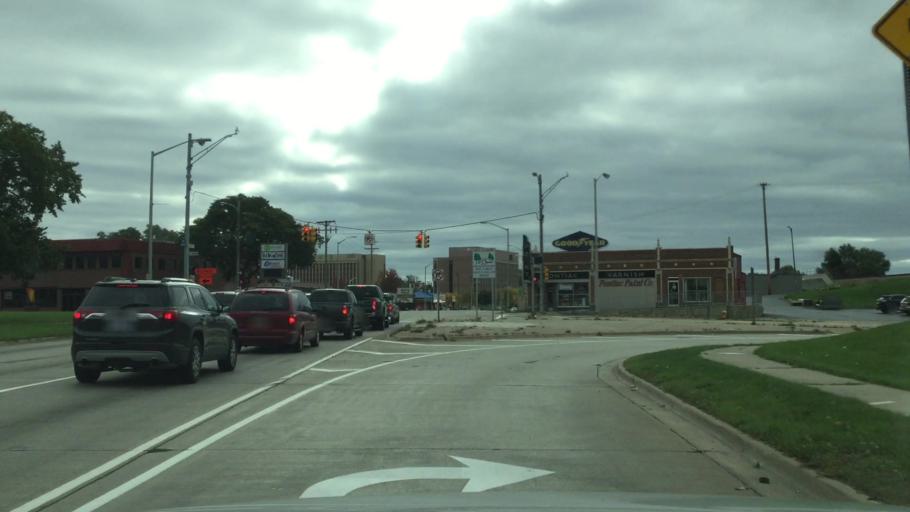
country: US
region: Michigan
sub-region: Oakland County
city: Pontiac
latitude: 42.6387
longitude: -83.2966
